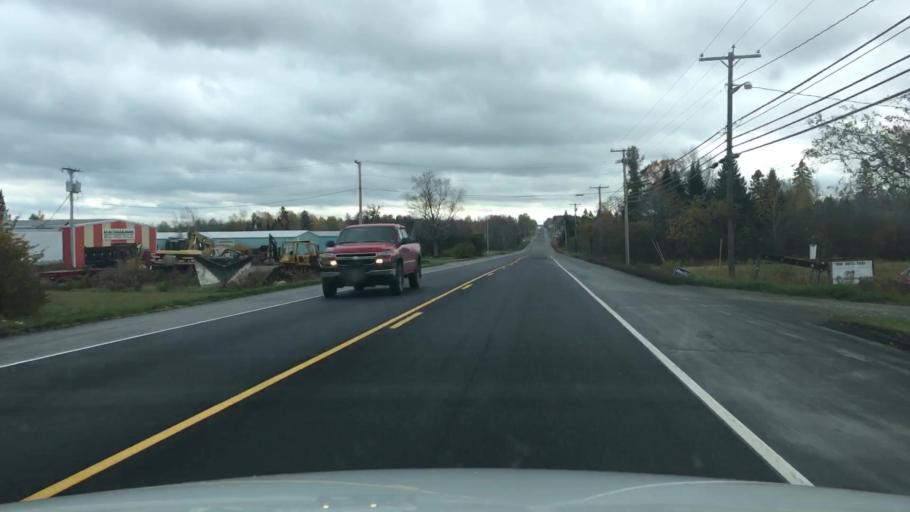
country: US
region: Maine
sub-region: Aroostook County
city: Houlton
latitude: 46.2481
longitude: -67.8408
